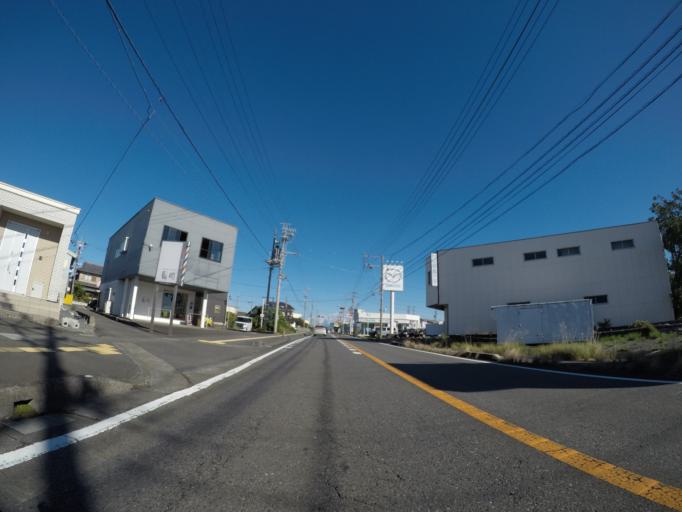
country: JP
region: Shizuoka
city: Sagara
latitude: 34.7446
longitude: 138.2374
